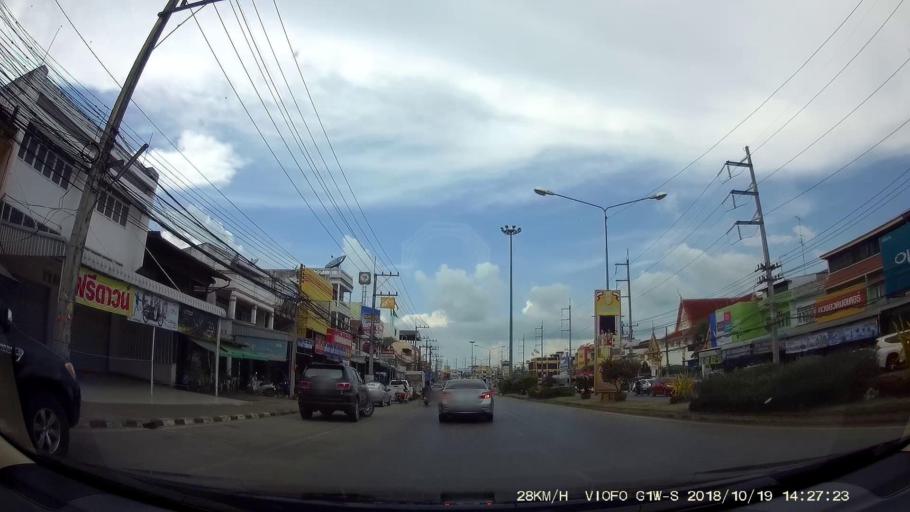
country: TH
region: Chaiyaphum
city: Kaeng Khro
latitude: 16.1112
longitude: 102.2580
